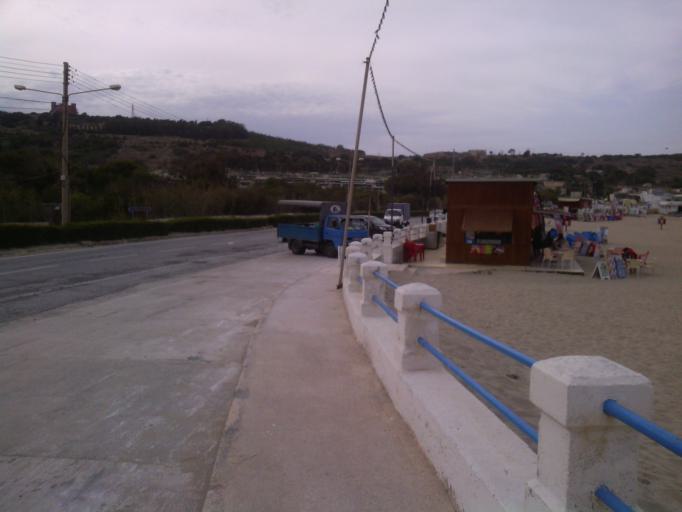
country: MT
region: Il-Mellieha
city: Mellieha
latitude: 35.9701
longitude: 14.3497
